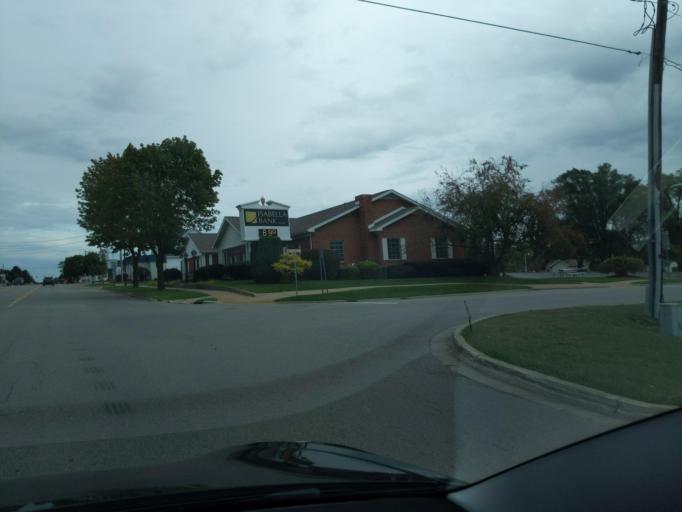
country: US
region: Michigan
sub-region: Clare County
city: Clare
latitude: 43.8354
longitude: -84.8712
